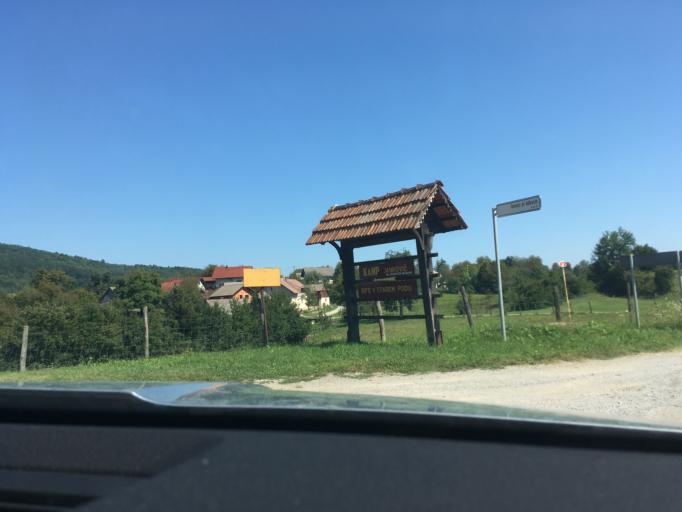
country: SI
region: Metlika
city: Metlika
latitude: 45.5205
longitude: 15.3143
